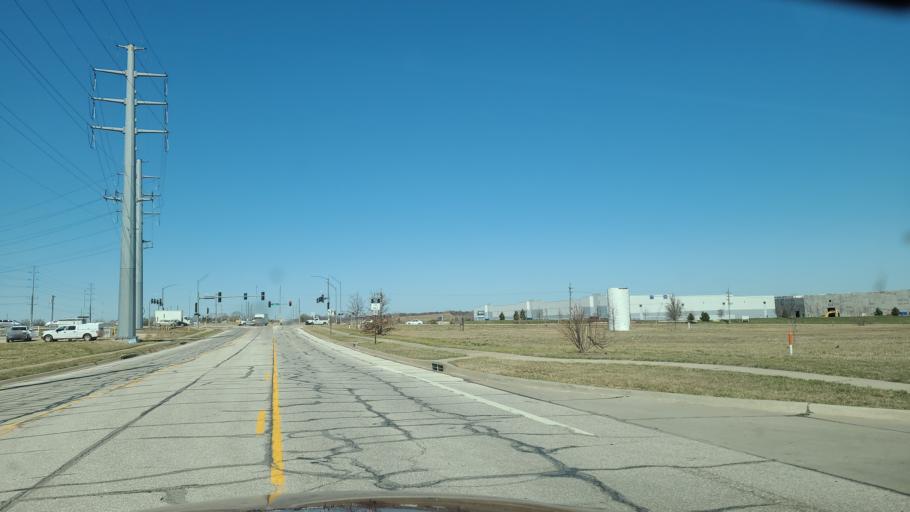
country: US
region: Kansas
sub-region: Douglas County
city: Lawrence
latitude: 38.9412
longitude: -95.2049
